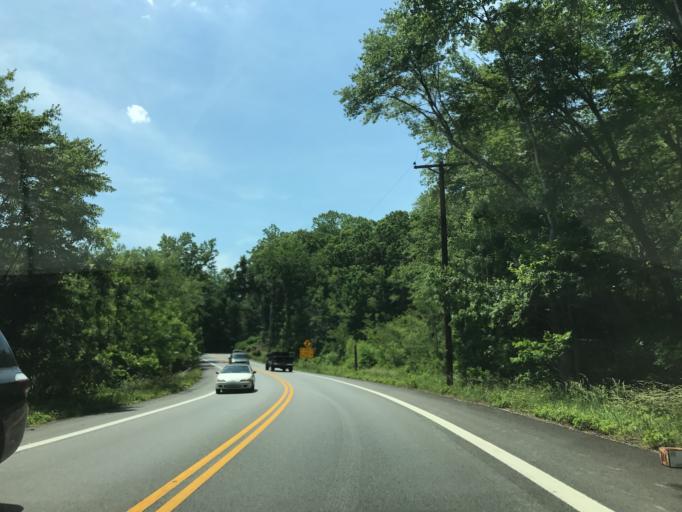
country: US
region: Maryland
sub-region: Anne Arundel County
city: Crownsville
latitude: 38.9860
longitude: -76.6178
